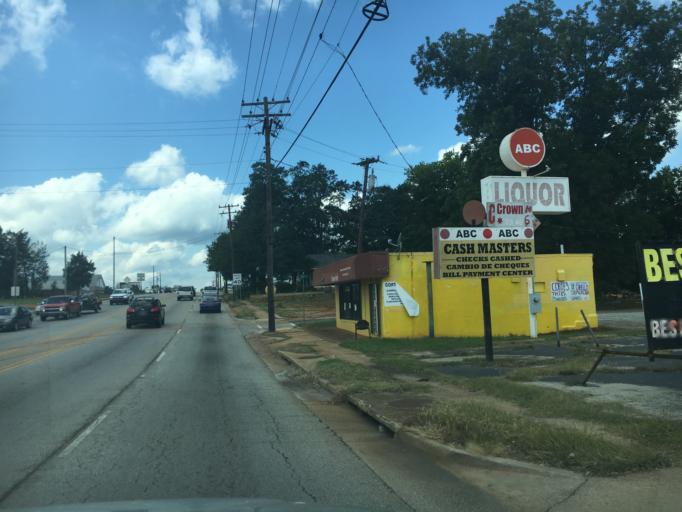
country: US
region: South Carolina
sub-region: Greenville County
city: Sans Souci
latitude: 34.8711
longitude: -82.4303
